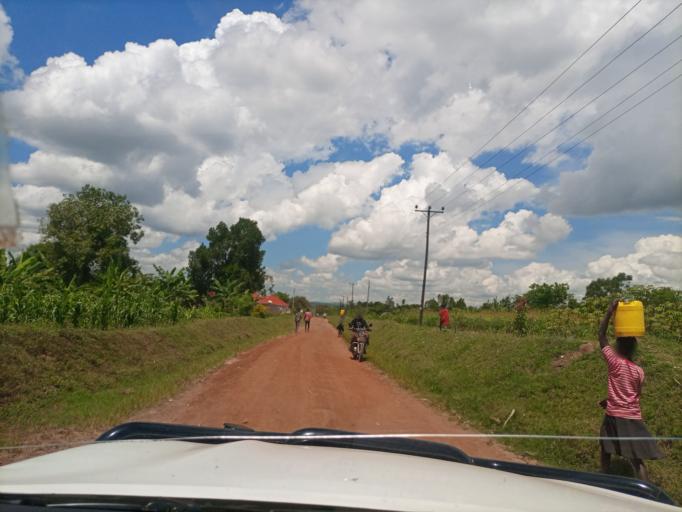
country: UG
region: Eastern Region
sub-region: Tororo District
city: Tororo
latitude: 0.6462
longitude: 33.9958
